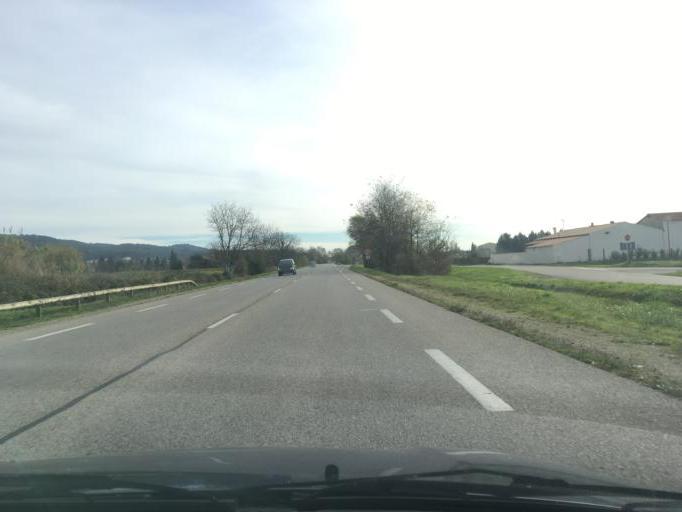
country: FR
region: Provence-Alpes-Cote d'Azur
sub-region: Departement du Vaucluse
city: Cadenet
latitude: 43.7311
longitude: 5.3628
